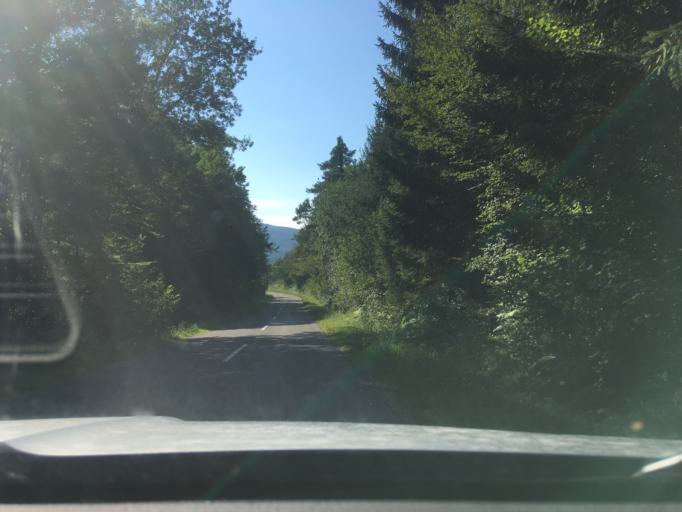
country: SI
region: Crnomelj
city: Crnomelj
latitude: 45.4573
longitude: 15.2279
